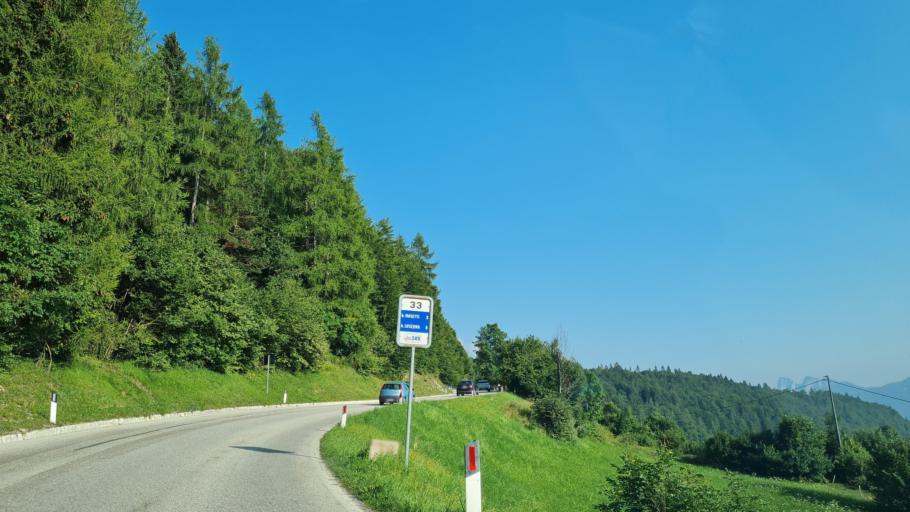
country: IT
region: Trentino-Alto Adige
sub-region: Provincia di Trento
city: Gionghi-Cappella
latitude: 45.9391
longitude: 11.2826
